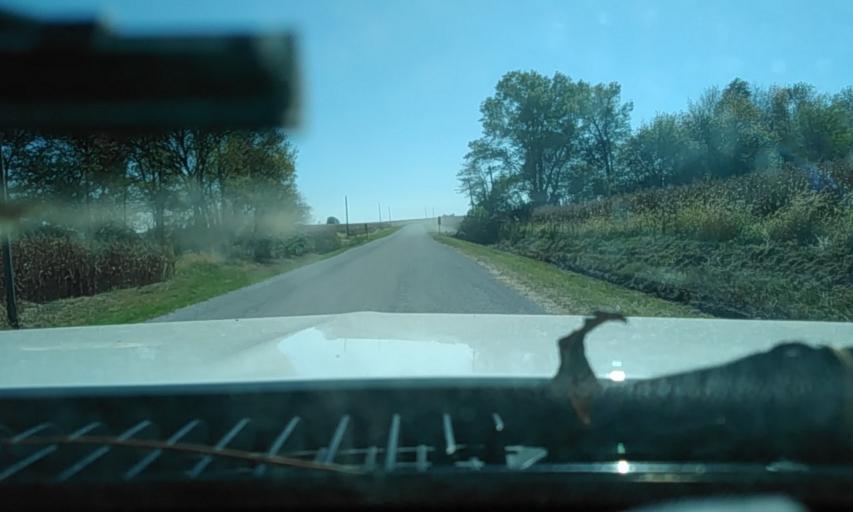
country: US
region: Illinois
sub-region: Bond County
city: Greenville
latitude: 39.0015
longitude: -89.3754
